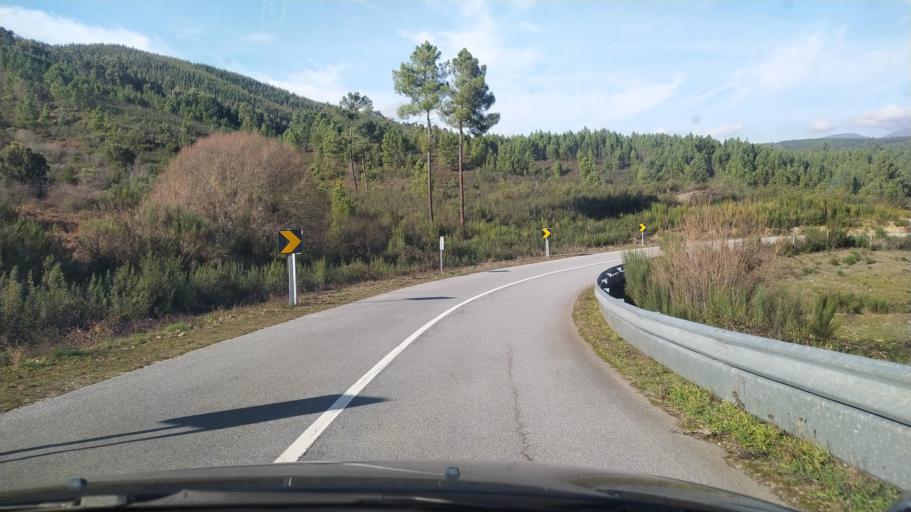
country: PT
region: Castelo Branco
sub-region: Concelho do Fundao
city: Aldeia de Joanes
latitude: 40.1773
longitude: -7.6749
